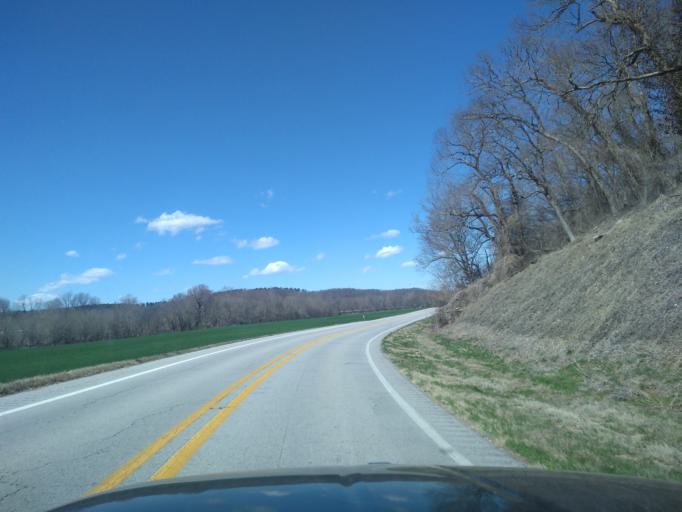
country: US
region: Arkansas
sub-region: Washington County
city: Farmington
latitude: 36.0982
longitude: -94.3399
